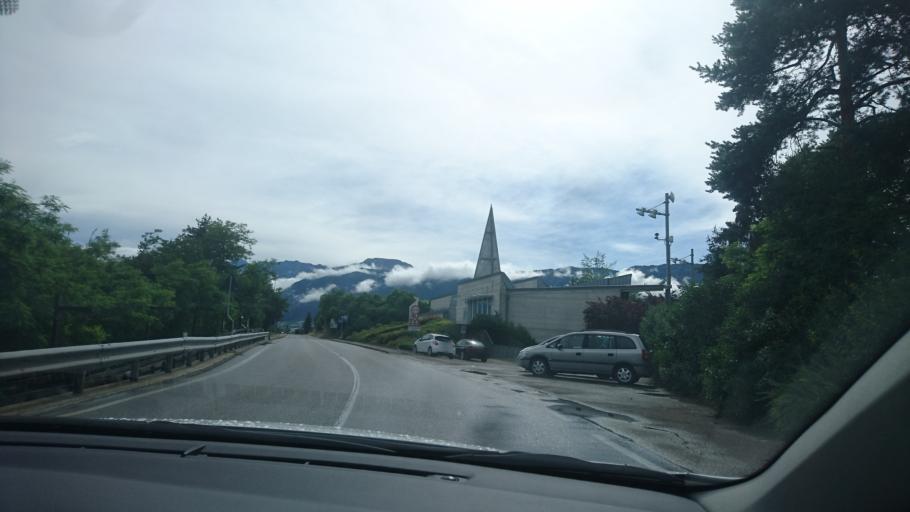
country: IT
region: Trentino-Alto Adige
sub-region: Provincia di Trento
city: Sanzeno
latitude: 46.3705
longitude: 11.0817
